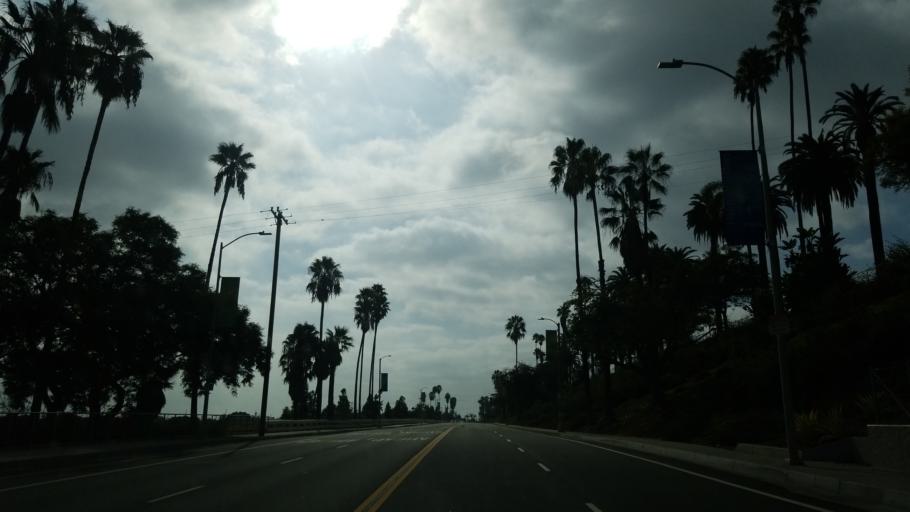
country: US
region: California
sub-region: Los Angeles County
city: San Pedro
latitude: 33.7356
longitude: -118.2800
